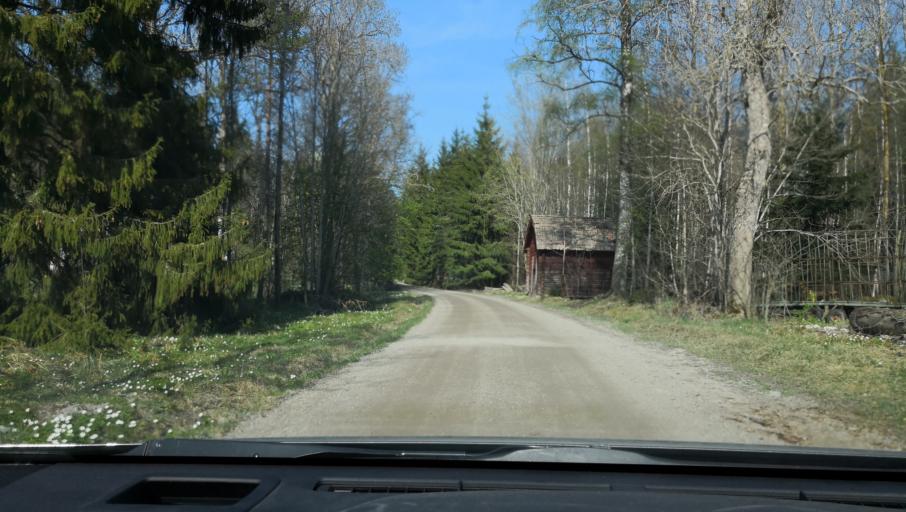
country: SE
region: Uppsala
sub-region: Heby Kommun
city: Heby
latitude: 60.0122
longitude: 16.7369
